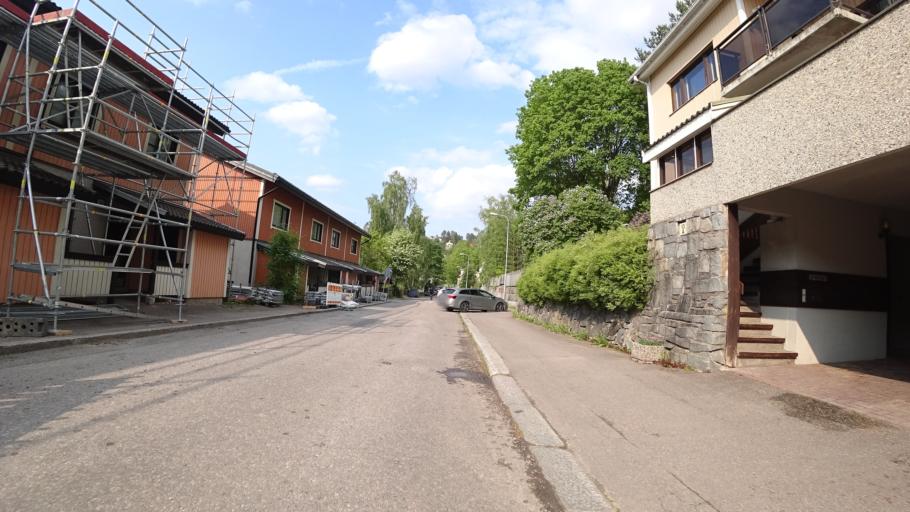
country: FI
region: Pirkanmaa
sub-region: Tampere
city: Tampere
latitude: 61.4972
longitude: 23.7134
